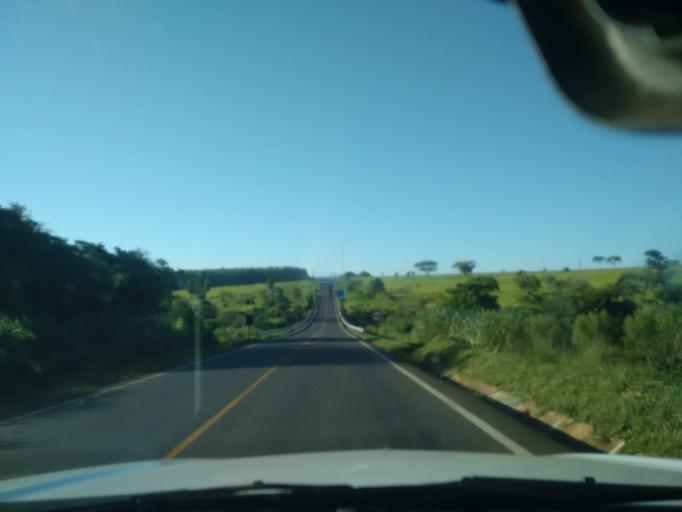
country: BR
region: Mato Grosso do Sul
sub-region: Eldorado
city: Eldorado
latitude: -23.8747
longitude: -54.3234
